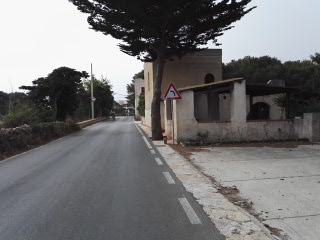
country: IT
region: Sicily
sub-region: Trapani
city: Favignana
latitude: 37.9239
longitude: 12.3367
